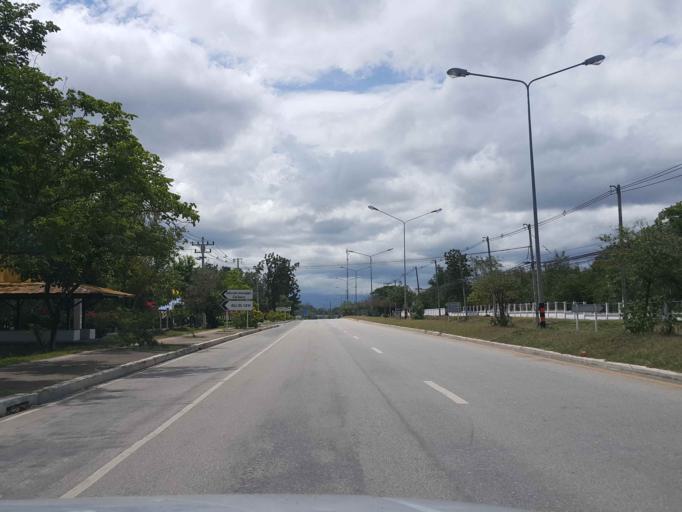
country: TH
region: Tak
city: Tak
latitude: 16.8813
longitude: 99.1379
